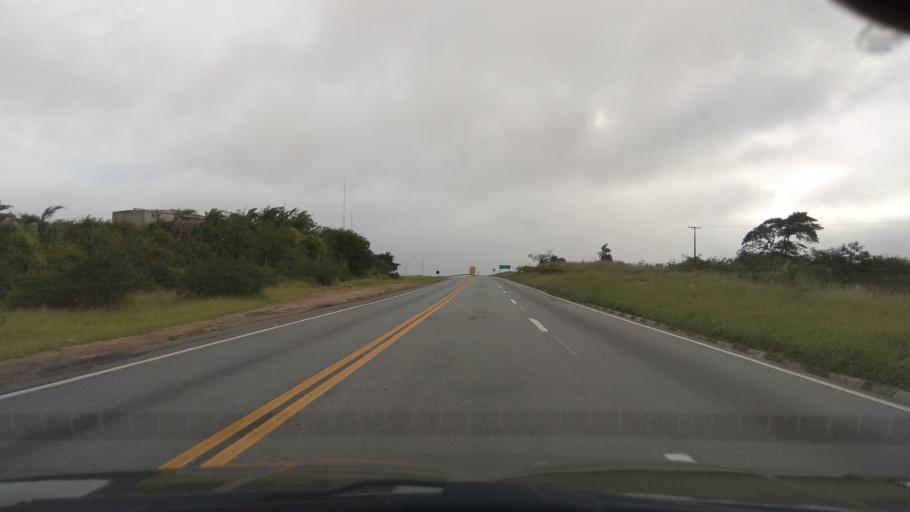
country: BR
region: Bahia
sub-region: Santa Ines
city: Santa Ines
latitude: -13.0648
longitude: -39.9585
